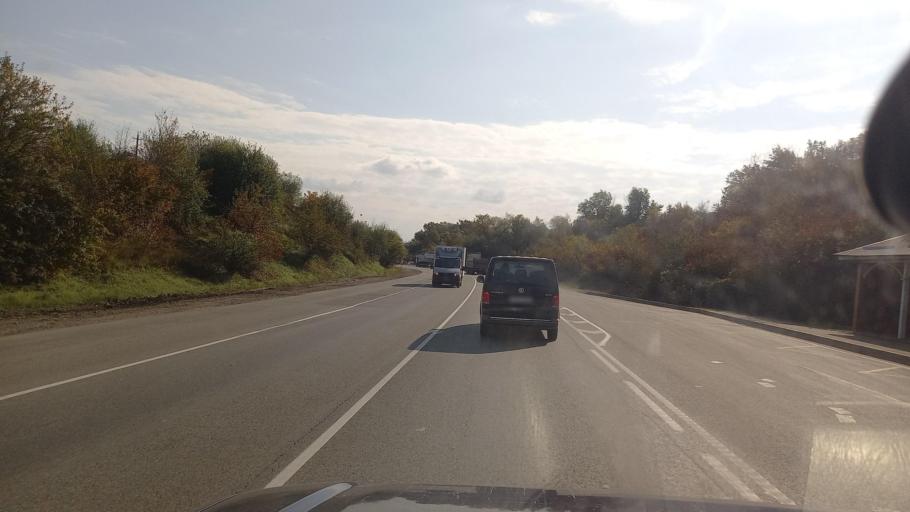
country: RU
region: Krasnodarskiy
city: Abinsk
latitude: 44.8498
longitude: 38.1369
